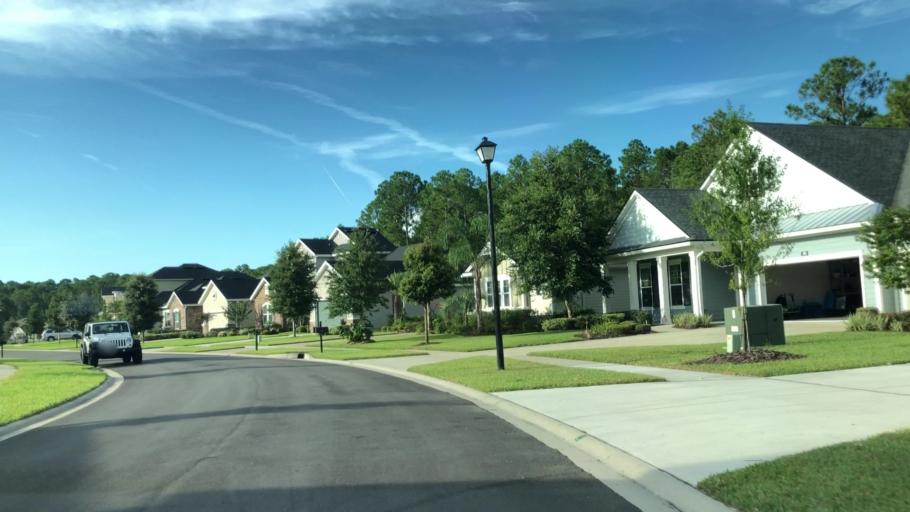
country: US
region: Florida
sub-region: Saint Johns County
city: Palm Valley
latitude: 30.1333
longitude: -81.4285
